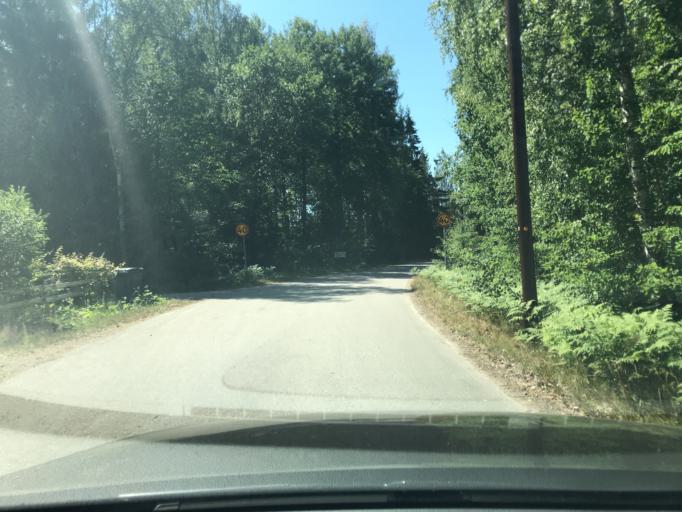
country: SE
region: Kronoberg
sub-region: Vaxjo Kommun
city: Vaexjoe
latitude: 56.9139
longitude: 14.8404
